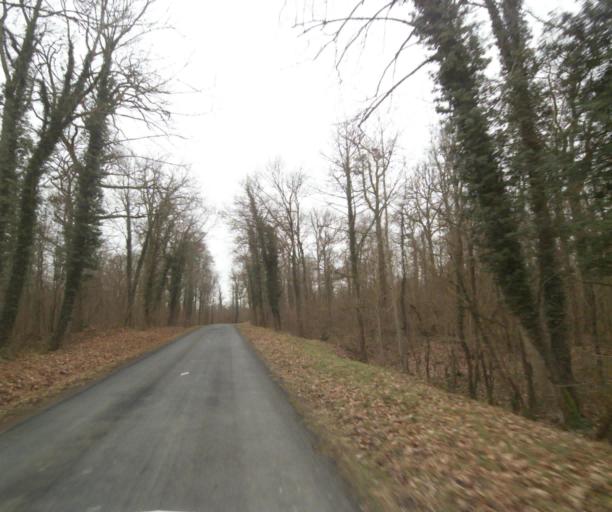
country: FR
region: Champagne-Ardenne
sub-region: Departement de la Haute-Marne
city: Bienville
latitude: 48.5670
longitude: 5.0176
